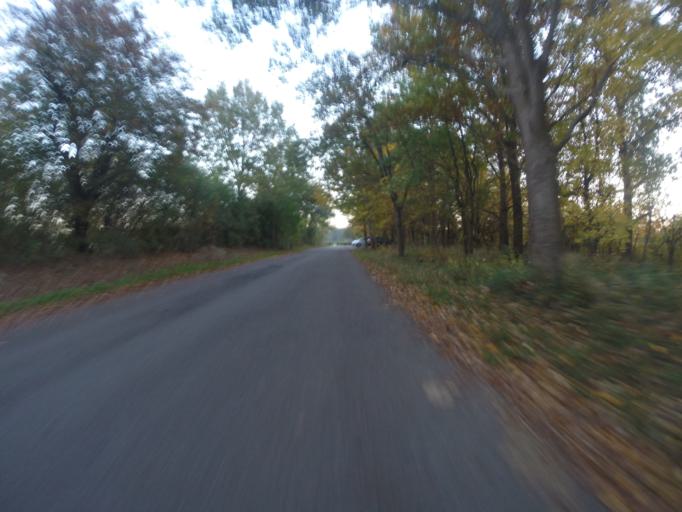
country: DK
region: Capital Region
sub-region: Hoje-Taastrup Kommune
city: Taastrup
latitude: 55.6685
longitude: 12.2978
